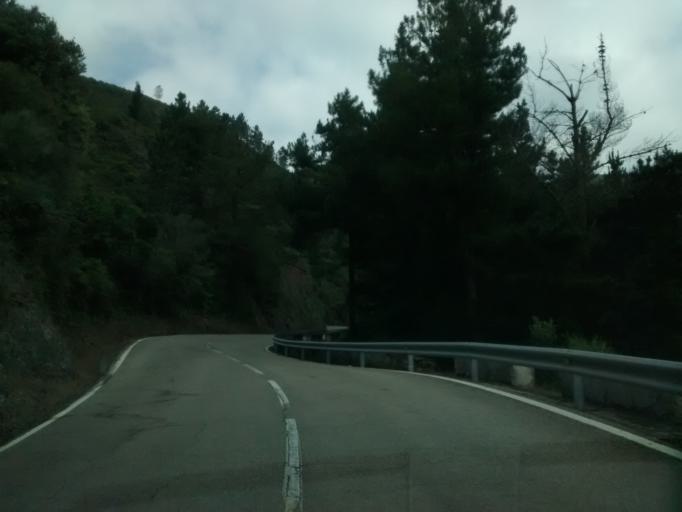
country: ES
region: Galicia
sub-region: Provincia de Ourense
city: Manzaneda
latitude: 42.3379
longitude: -7.2036
